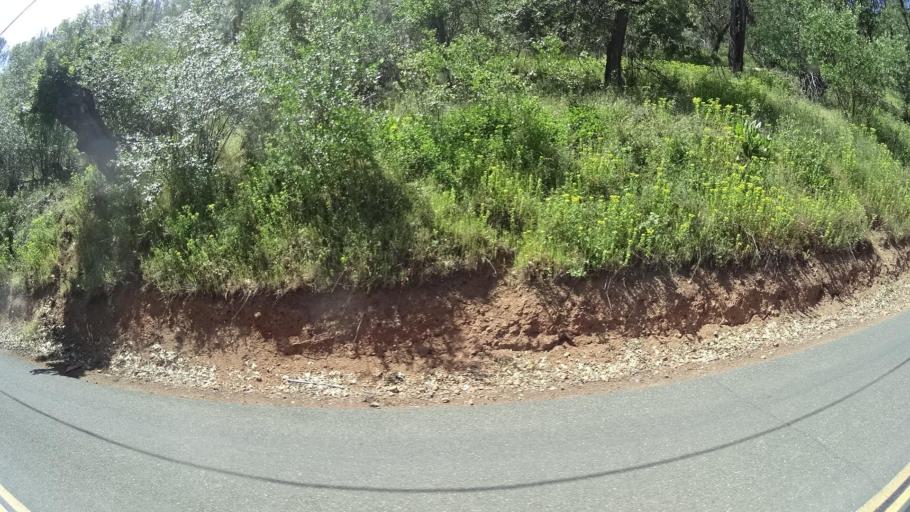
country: US
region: California
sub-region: Lake County
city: Clearlake
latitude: 38.9441
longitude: -122.6786
